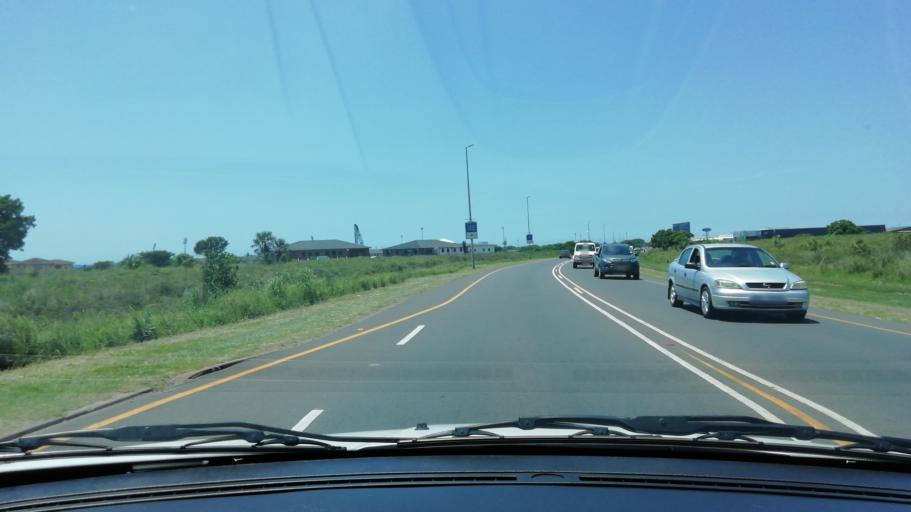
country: ZA
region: KwaZulu-Natal
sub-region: uThungulu District Municipality
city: Richards Bay
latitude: -28.7404
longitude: 32.0476
